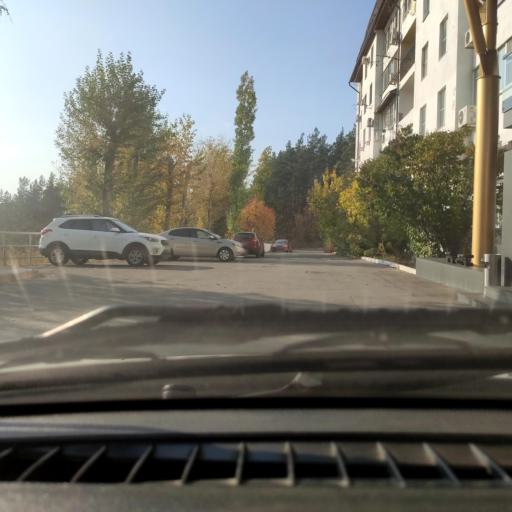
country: RU
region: Samara
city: Tol'yatti
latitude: 53.4744
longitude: 49.3545
